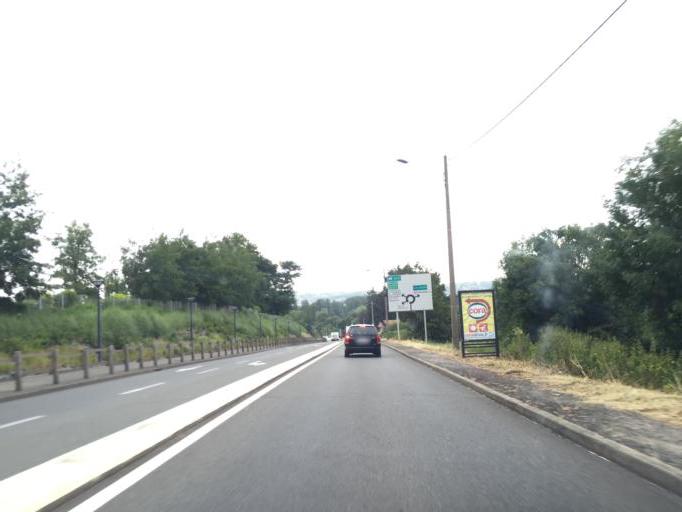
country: FR
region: Auvergne
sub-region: Departement de l'Allier
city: Bellerive-sur-Allier
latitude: 46.1268
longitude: 3.3969
